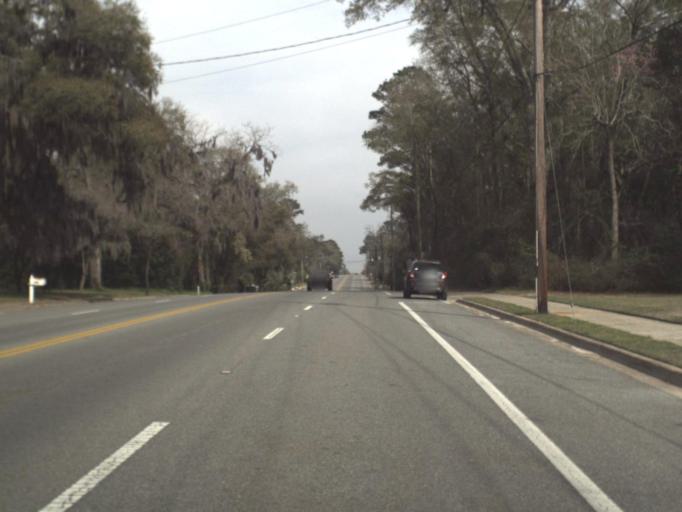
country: US
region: Florida
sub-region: Jefferson County
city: Monticello
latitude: 30.5451
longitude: -83.8623
